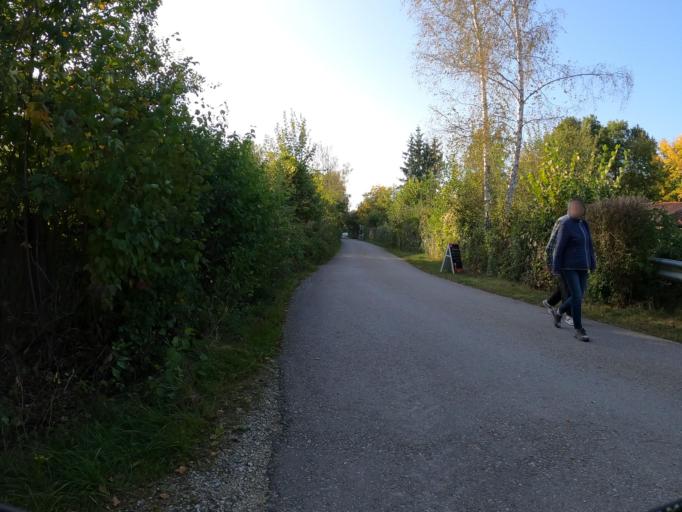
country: DE
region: Bavaria
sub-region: Swabia
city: Nersingen
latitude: 48.4466
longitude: 10.1277
